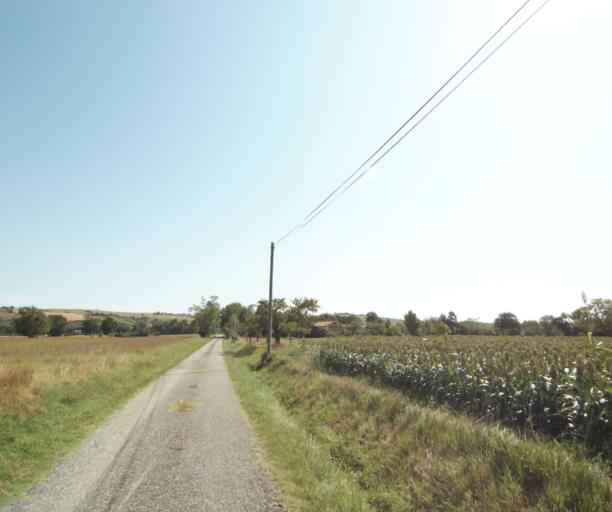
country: FR
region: Midi-Pyrenees
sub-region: Departement de l'Ariege
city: Lezat-sur-Leze
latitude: 43.2935
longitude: 1.3381
